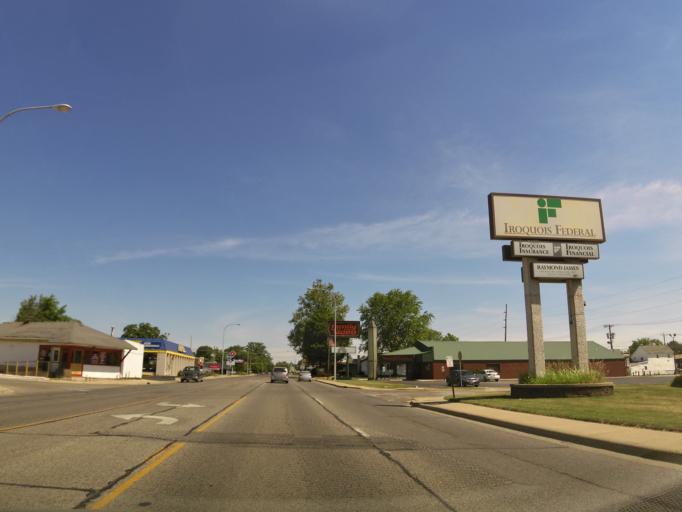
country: US
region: Illinois
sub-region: Vermilion County
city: Danville
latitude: 40.1355
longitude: -87.6355
